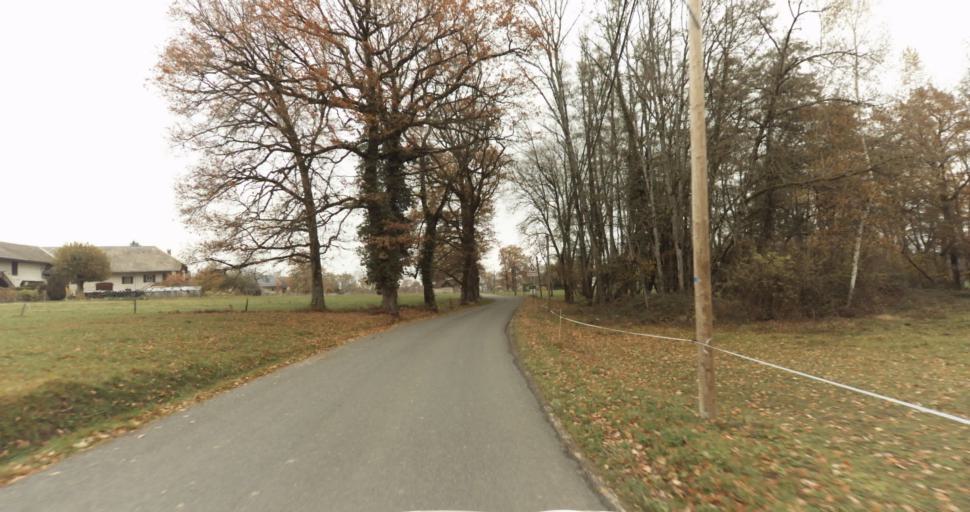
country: FR
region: Rhone-Alpes
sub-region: Departement de la Haute-Savoie
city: Cusy
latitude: 45.7770
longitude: 6.0081
